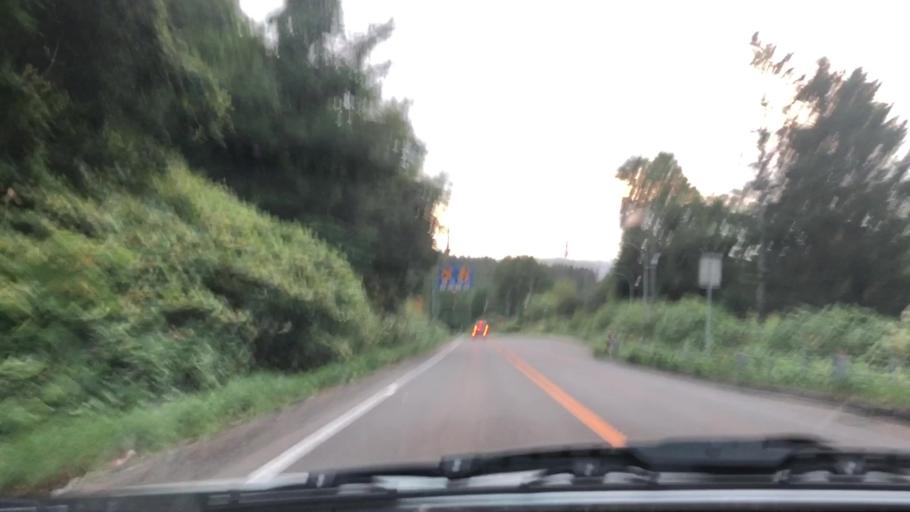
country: JP
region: Hokkaido
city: Iwamizawa
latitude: 42.9291
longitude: 142.1027
